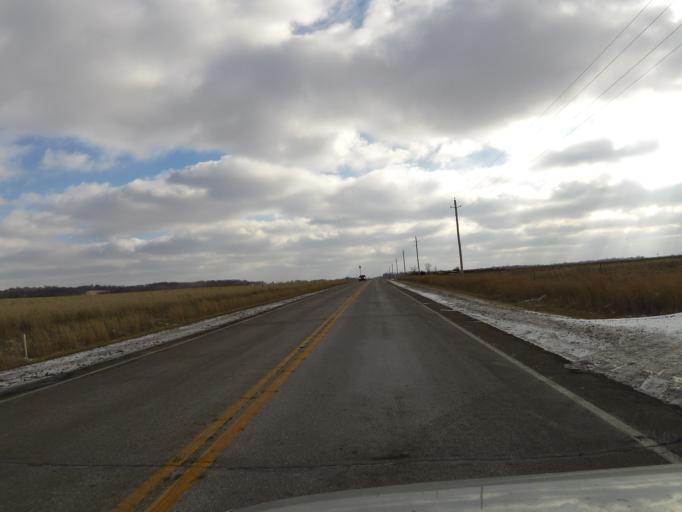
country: US
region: Minnesota
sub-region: Scott County
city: Prior Lake
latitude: 44.7685
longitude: -93.4495
